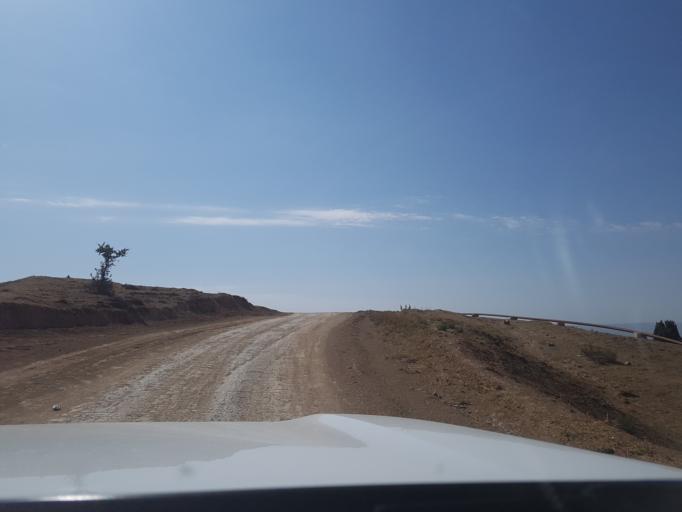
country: TM
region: Ahal
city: Baharly
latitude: 38.3221
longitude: 56.9530
